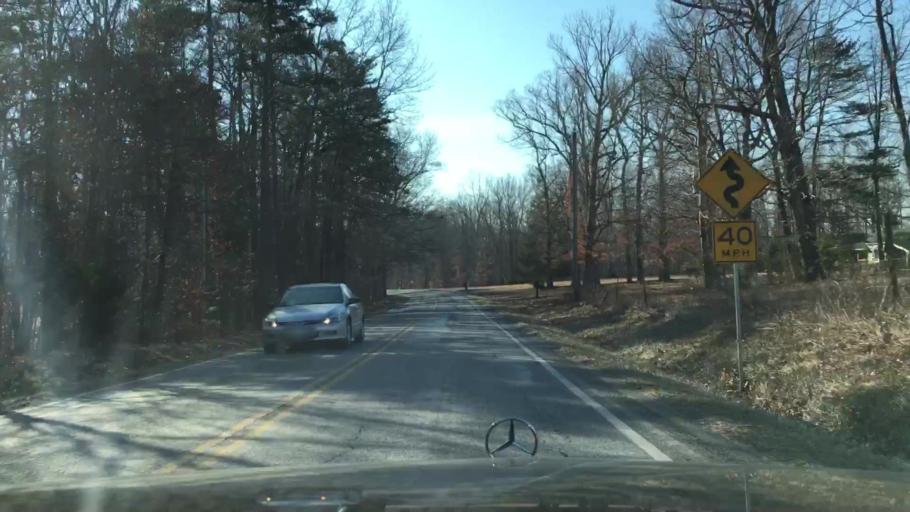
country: US
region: Virginia
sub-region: Pittsylvania County
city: Motley
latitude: 37.1739
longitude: -79.4081
